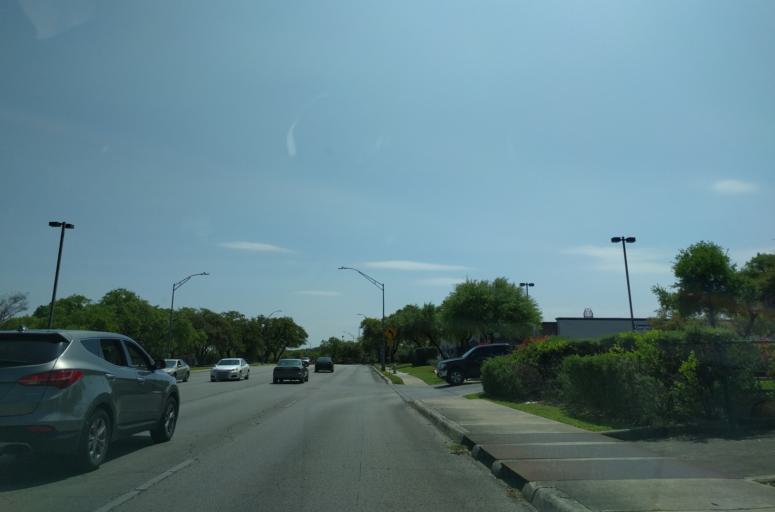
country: US
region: Texas
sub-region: Bexar County
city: Shavano Park
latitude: 29.5642
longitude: -98.5859
